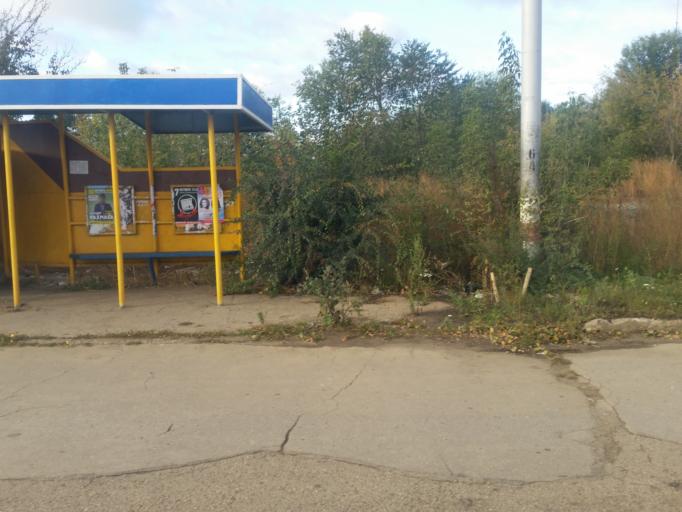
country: RU
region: Ulyanovsk
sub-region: Ulyanovskiy Rayon
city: Ulyanovsk
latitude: 54.3158
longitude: 48.3853
